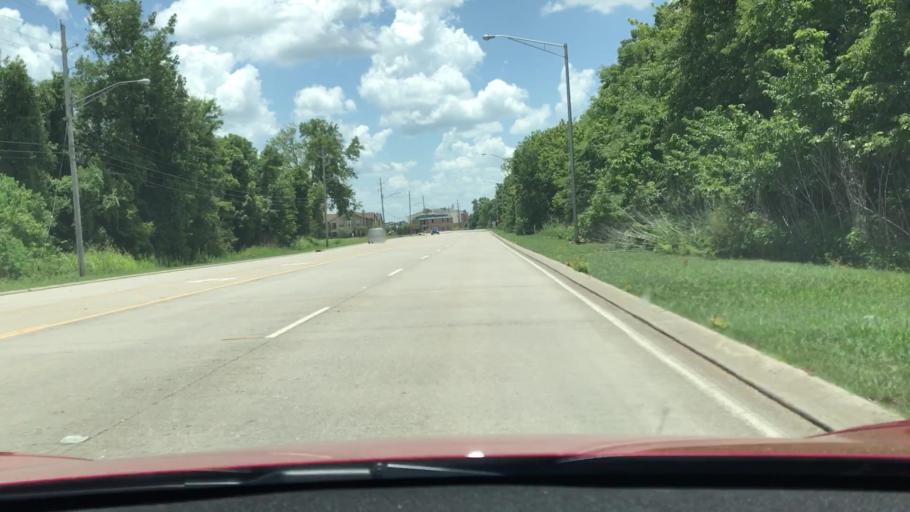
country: US
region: Louisiana
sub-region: Bossier Parish
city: Bossier City
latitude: 32.4298
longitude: -93.7256
